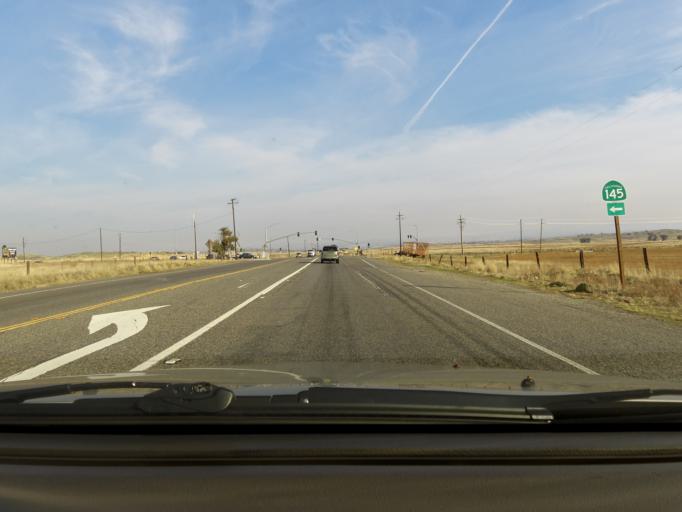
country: US
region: California
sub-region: Madera County
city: Bonadelle Ranchos-Madera Ranchos
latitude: 37.0088
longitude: -119.7939
